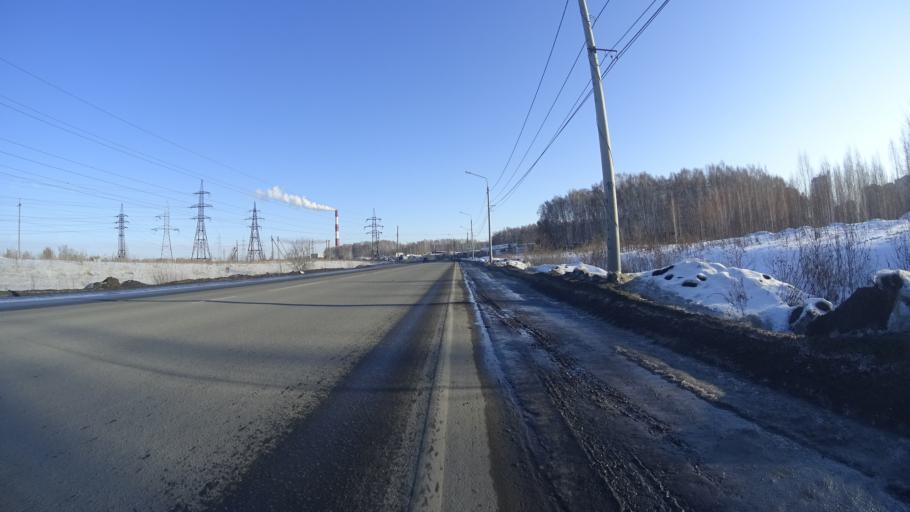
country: RU
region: Chelyabinsk
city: Roshchino
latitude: 55.2125
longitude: 61.3073
